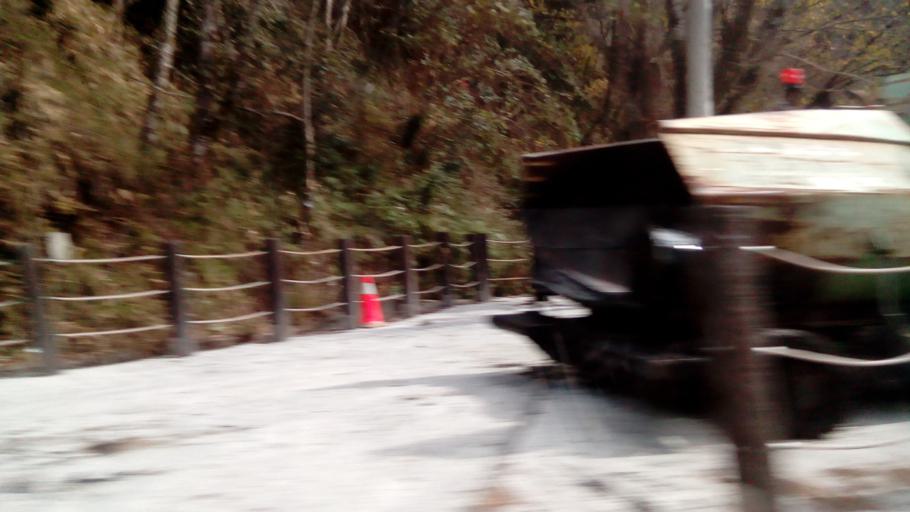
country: TW
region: Taiwan
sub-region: Hualien
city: Hualian
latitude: 24.3566
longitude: 121.3257
